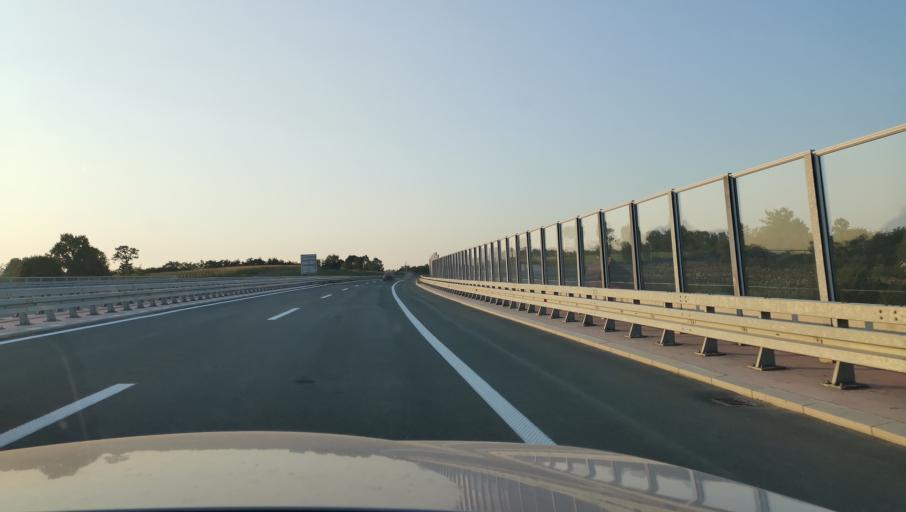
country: RS
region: Central Serbia
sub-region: Kolubarski Okrug
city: Lajkovac
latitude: 44.3636
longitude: 20.1214
